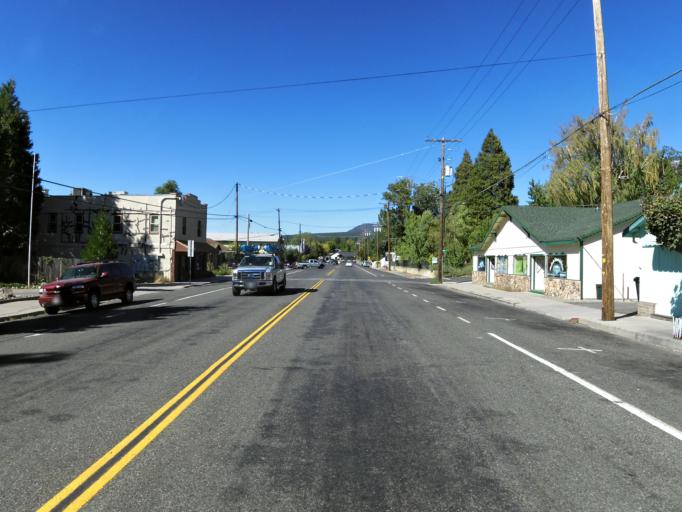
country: US
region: California
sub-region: Siskiyou County
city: Mount Shasta
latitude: 41.3100
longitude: -122.3110
